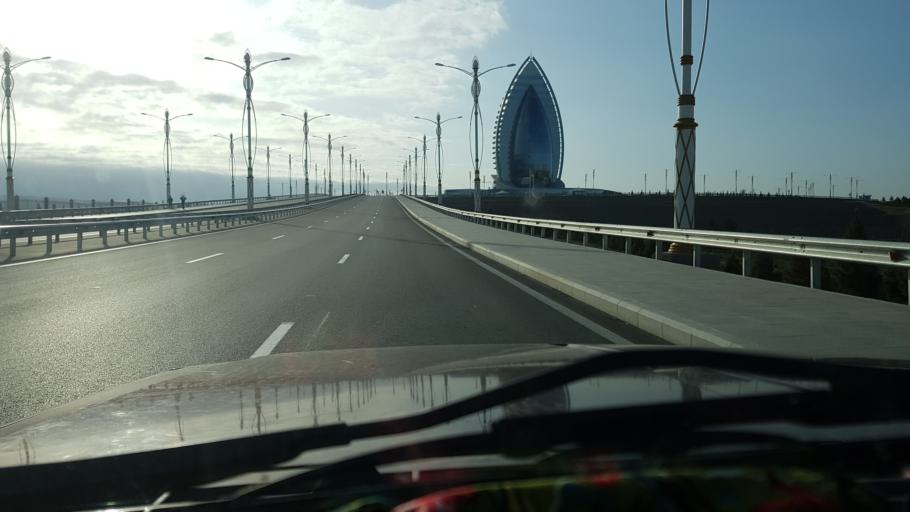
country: TM
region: Ahal
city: Ashgabat
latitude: 37.9271
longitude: 58.3396
